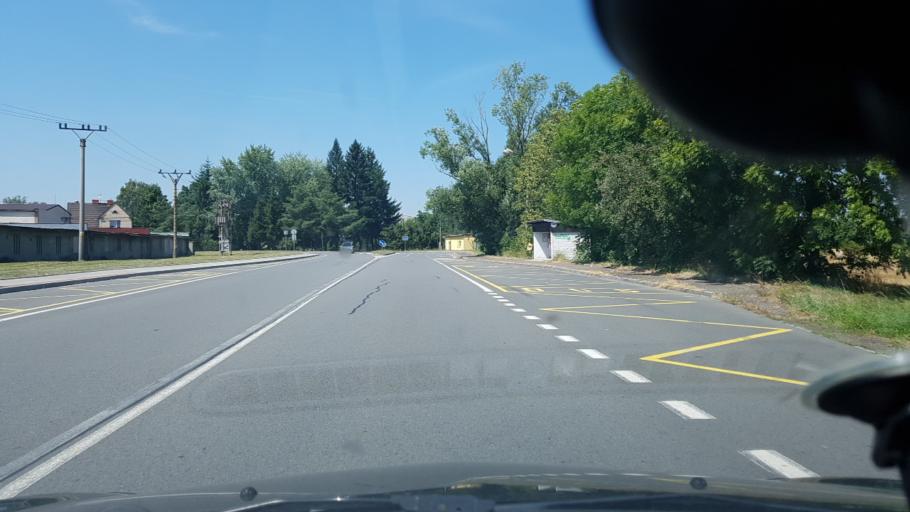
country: CZ
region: Moravskoslezsky
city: Stary Bohumin
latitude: 49.8961
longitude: 18.3344
